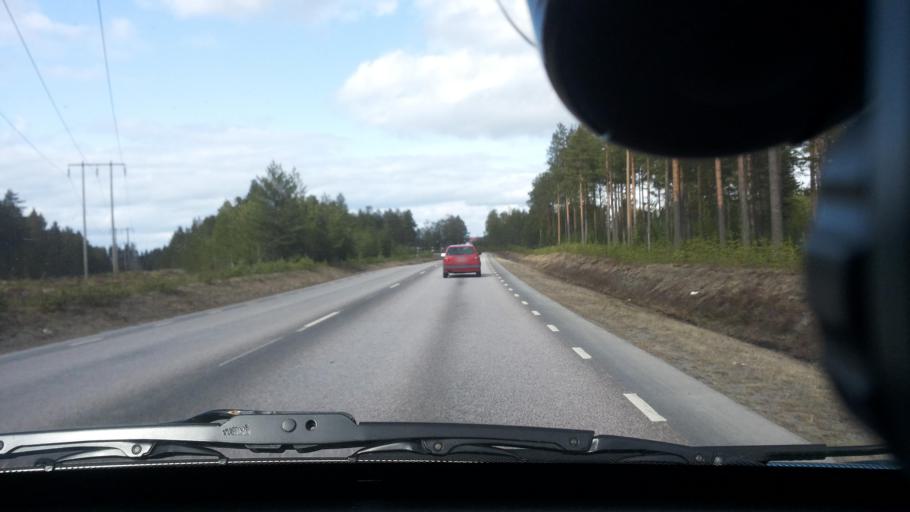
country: SE
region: Norrbotten
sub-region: Lulea Kommun
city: Gammelstad
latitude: 65.6097
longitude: 22.0403
